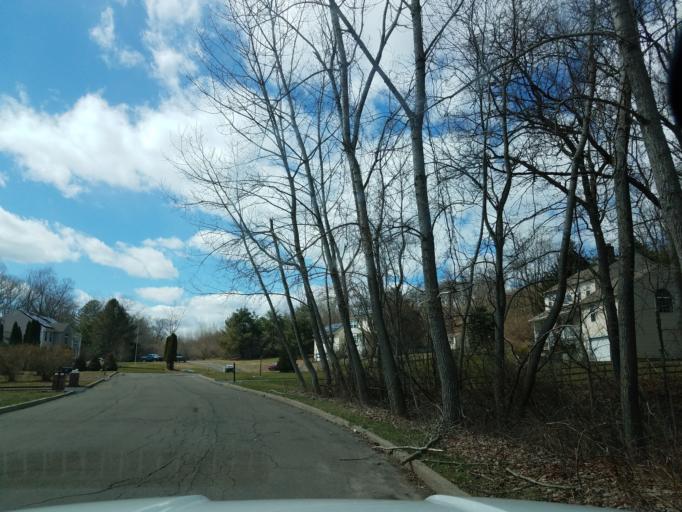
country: US
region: Connecticut
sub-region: New Haven County
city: Naugatuck
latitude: 41.4716
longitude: -73.0242
